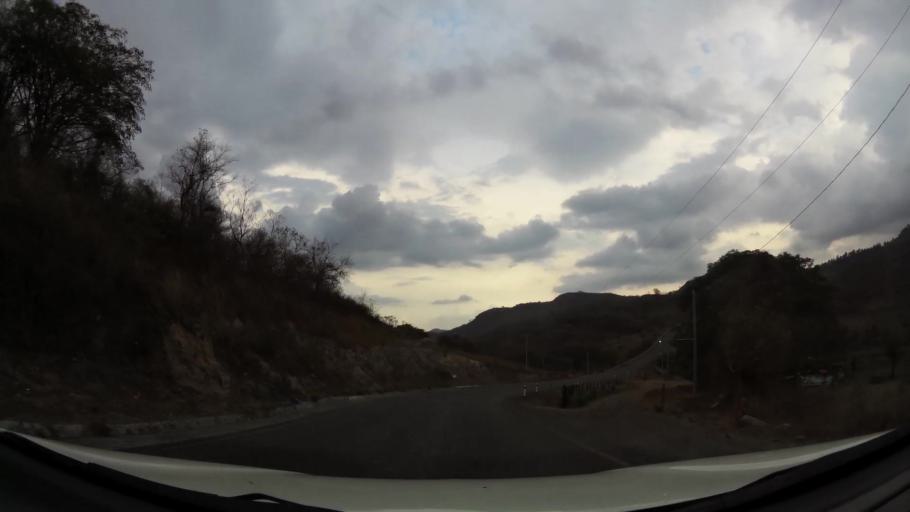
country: NI
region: Jinotega
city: Jinotega
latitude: 13.0275
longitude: -86.0021
